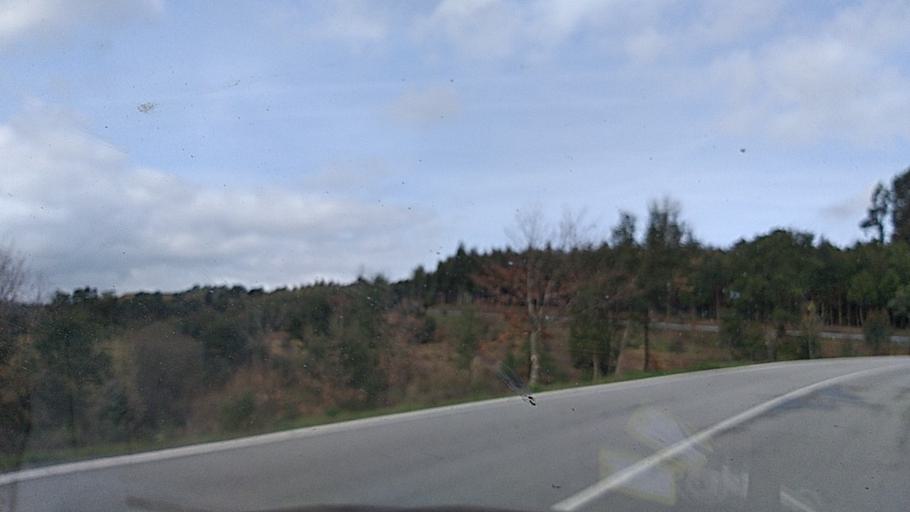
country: PT
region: Viseu
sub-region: Satao
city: Satao
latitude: 40.6672
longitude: -7.6845
